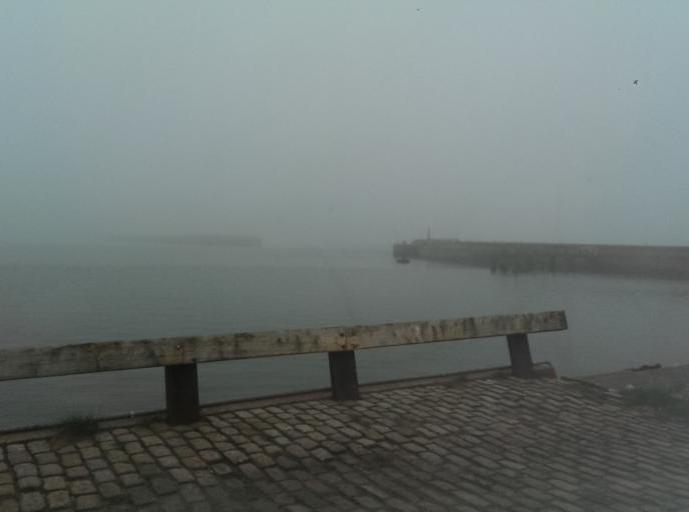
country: DK
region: South Denmark
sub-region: Esbjerg Kommune
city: Esbjerg
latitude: 55.4705
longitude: 8.4252
